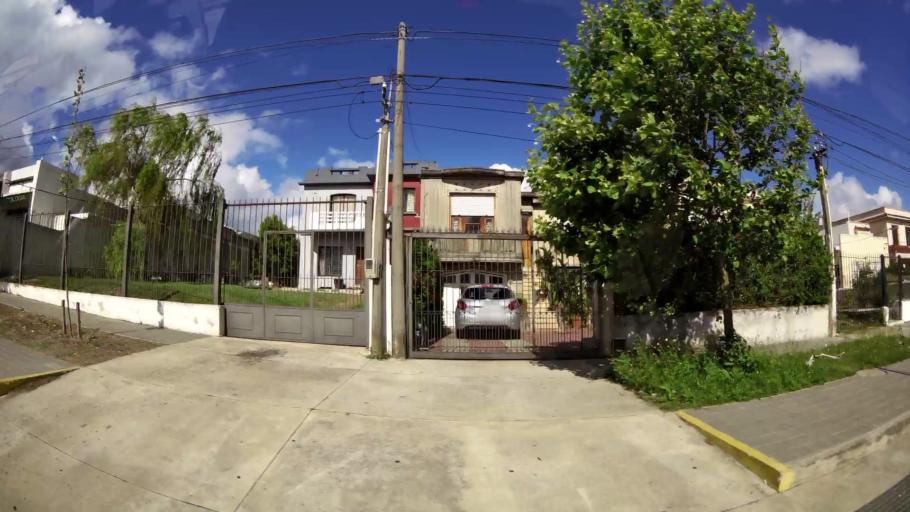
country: UY
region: Canelones
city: La Paz
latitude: -34.8245
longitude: -56.2197
